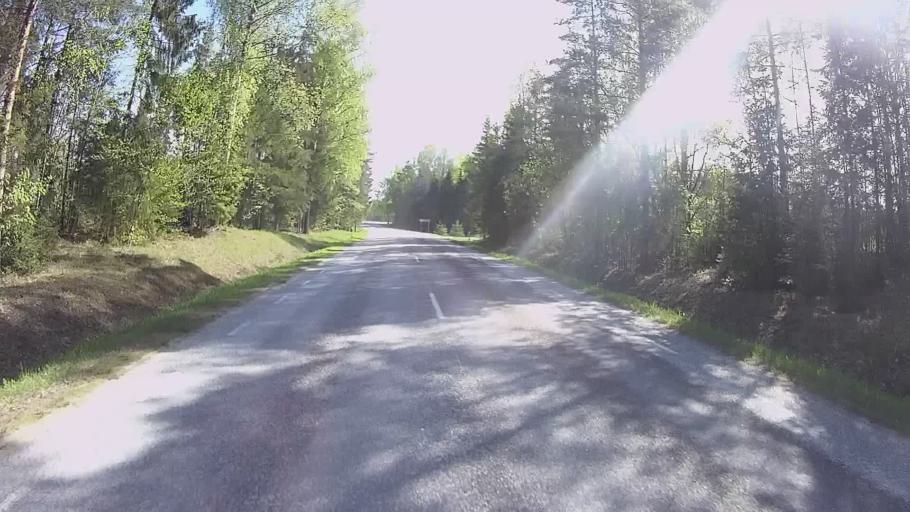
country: EE
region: Vorumaa
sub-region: Antsla vald
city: Vana-Antsla
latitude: 57.9986
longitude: 26.4962
